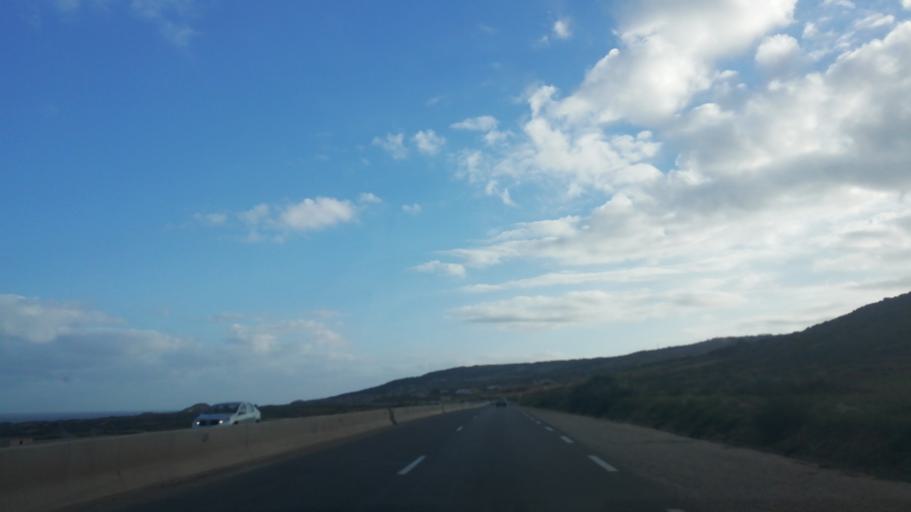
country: DZ
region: Mostaganem
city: Mostaganem
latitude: 36.0881
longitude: 0.1983
